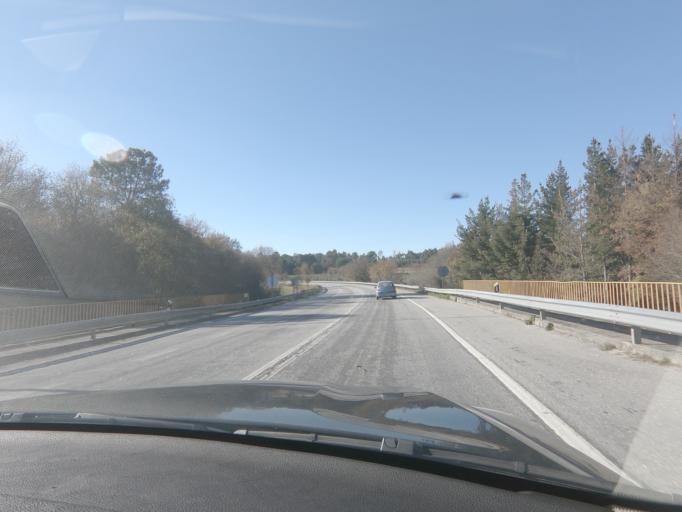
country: PT
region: Viseu
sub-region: Viseu
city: Abraveses
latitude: 40.6749
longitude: -7.9775
